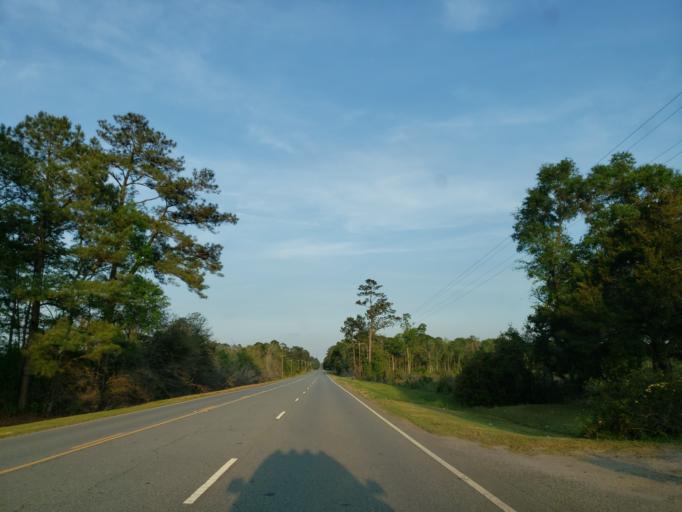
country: US
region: Georgia
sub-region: Lowndes County
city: Hahira
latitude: 30.9954
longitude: -83.4219
